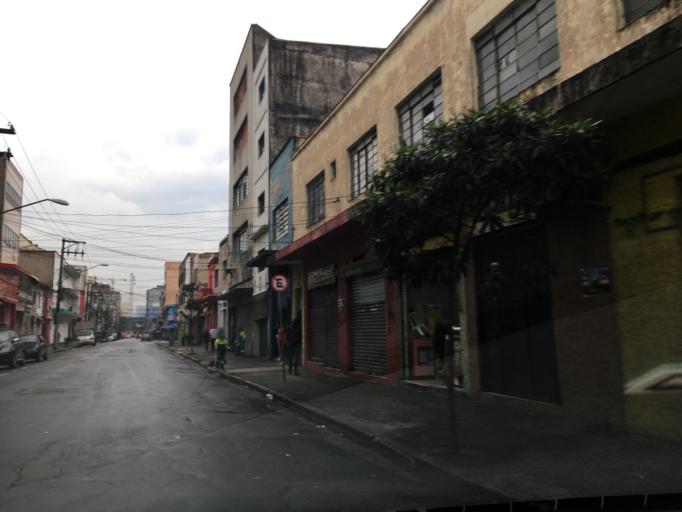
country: BR
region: Sao Paulo
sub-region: Sao Paulo
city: Sao Paulo
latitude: -23.5416
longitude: -46.6122
